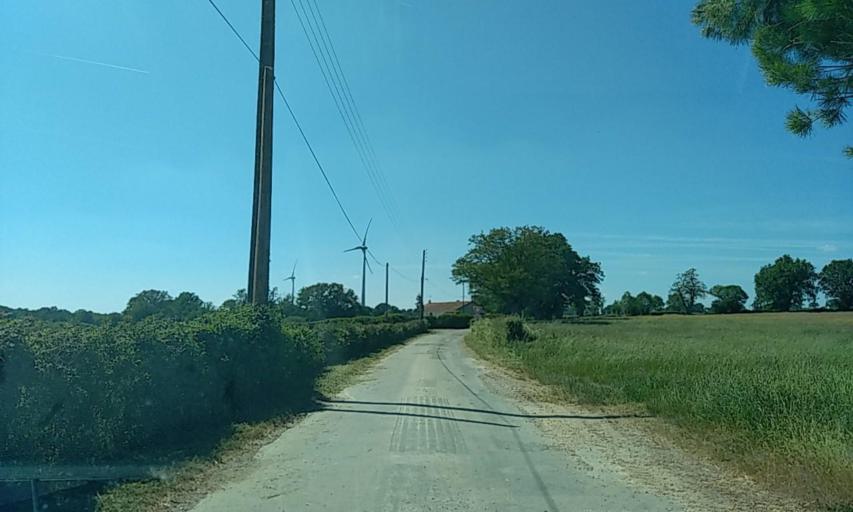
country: FR
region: Poitou-Charentes
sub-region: Departement des Deux-Sevres
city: La Chapelle-Saint-Laurent
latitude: 46.7863
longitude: -0.4770
